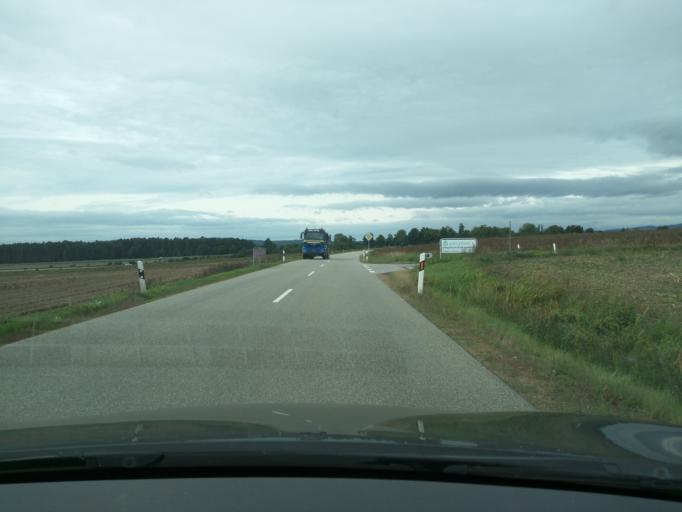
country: DE
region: Bavaria
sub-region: Upper Palatinate
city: Schwarzenfeld
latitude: 49.3571
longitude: 12.1569
